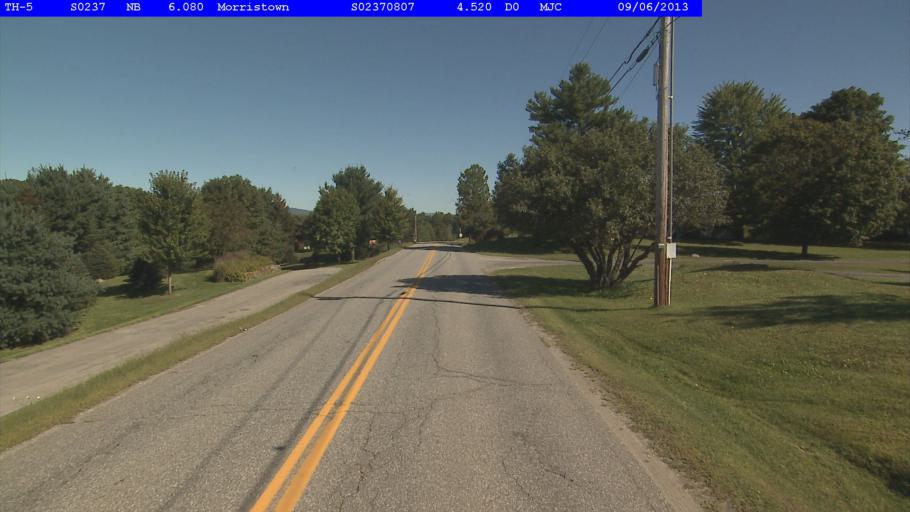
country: US
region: Vermont
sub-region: Lamoille County
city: Morristown
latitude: 44.5608
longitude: -72.6222
